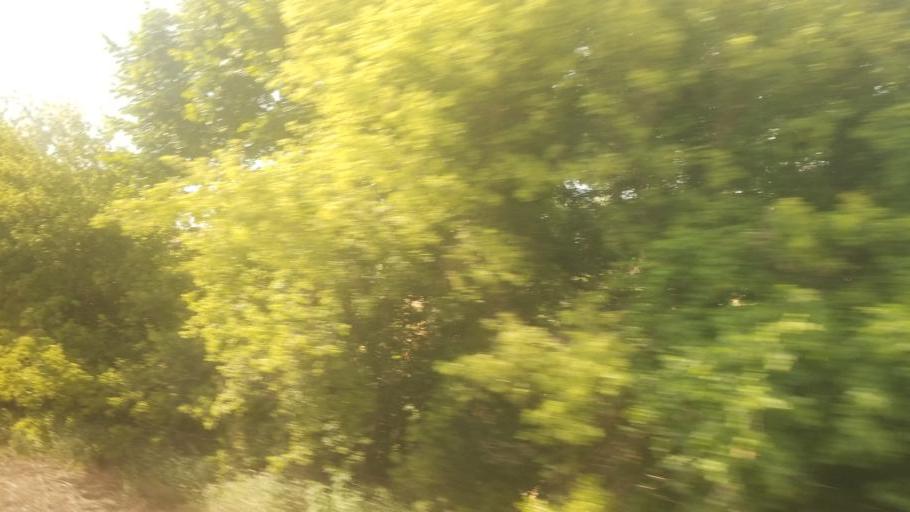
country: US
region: Kansas
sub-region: Johnson County
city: De Soto
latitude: 38.9797
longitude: -94.9267
